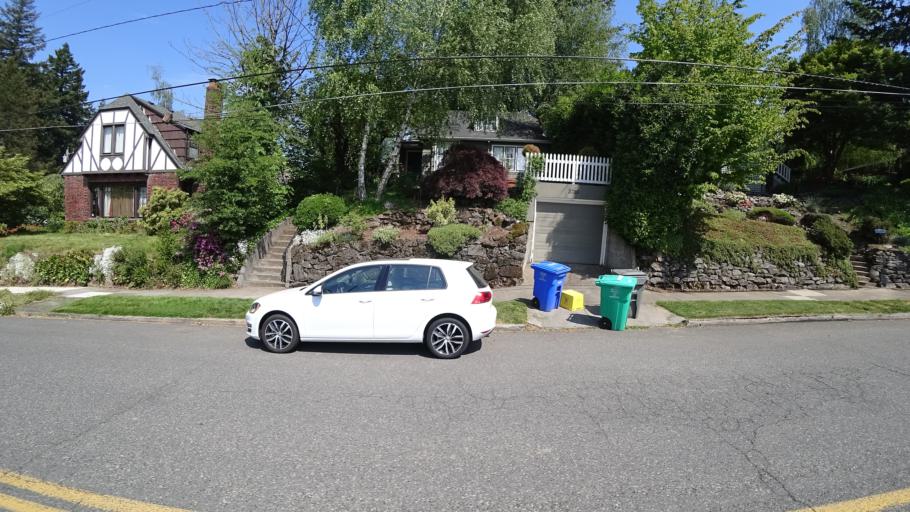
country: US
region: Oregon
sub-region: Multnomah County
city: Portland
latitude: 45.4959
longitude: -122.7019
